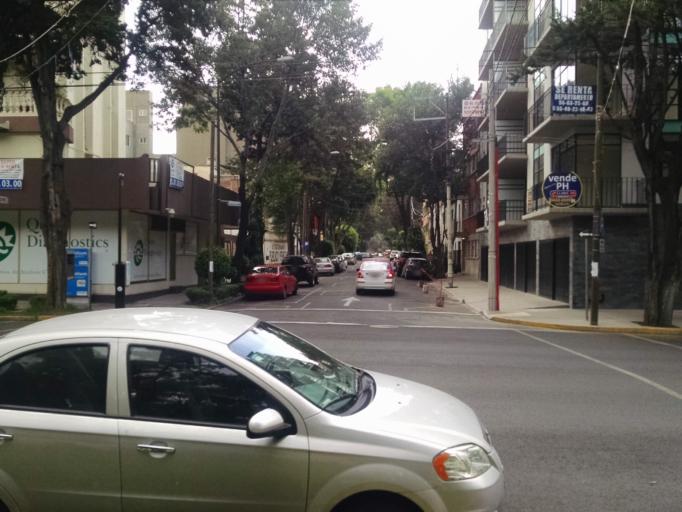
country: MX
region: Mexico City
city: Colonia del Valle
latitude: 19.3793
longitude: -99.1791
